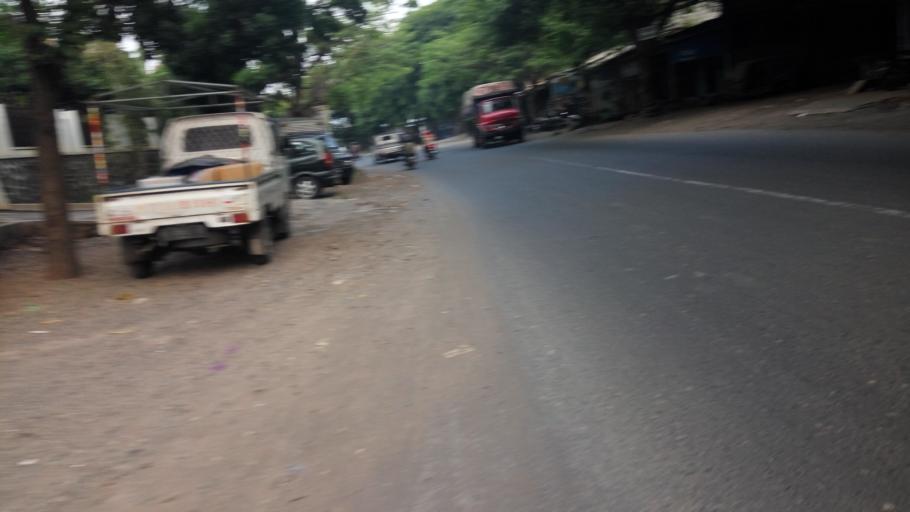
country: ID
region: Central Java
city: Semarang
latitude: -7.0032
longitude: 110.3946
